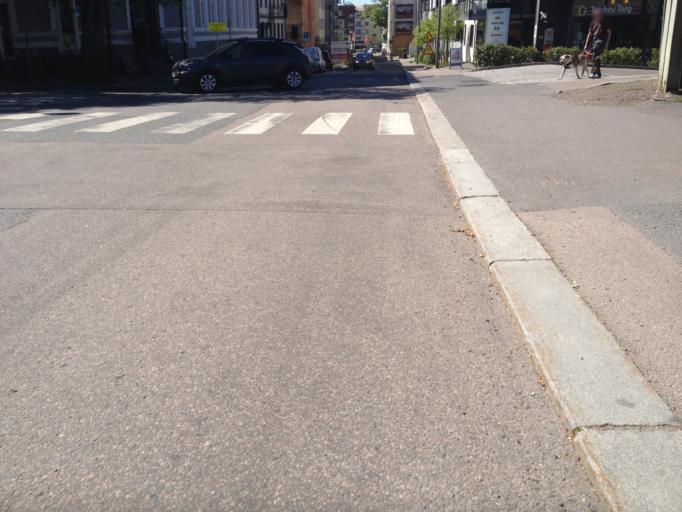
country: NO
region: Oslo
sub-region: Oslo
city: Oslo
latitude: 59.9345
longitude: 10.7622
